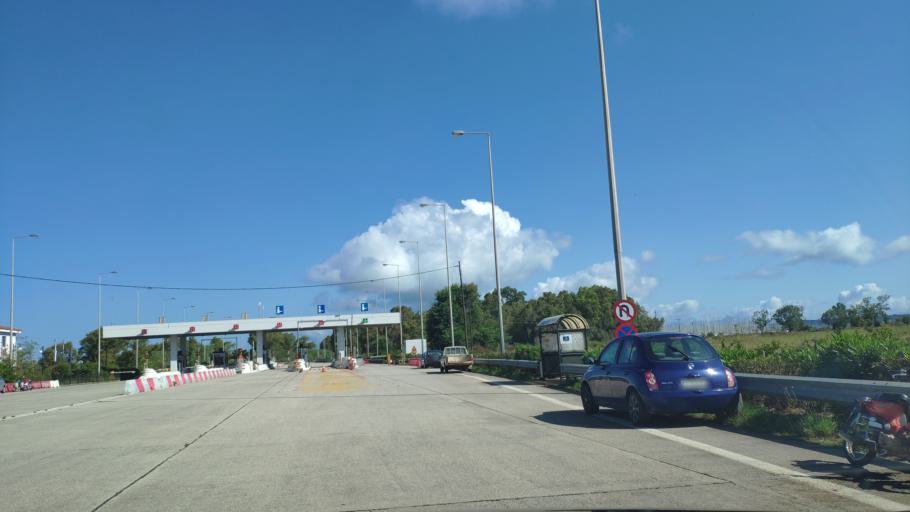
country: GR
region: Epirus
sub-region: Nomos Prevezis
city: Preveza
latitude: 38.9392
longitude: 20.7669
